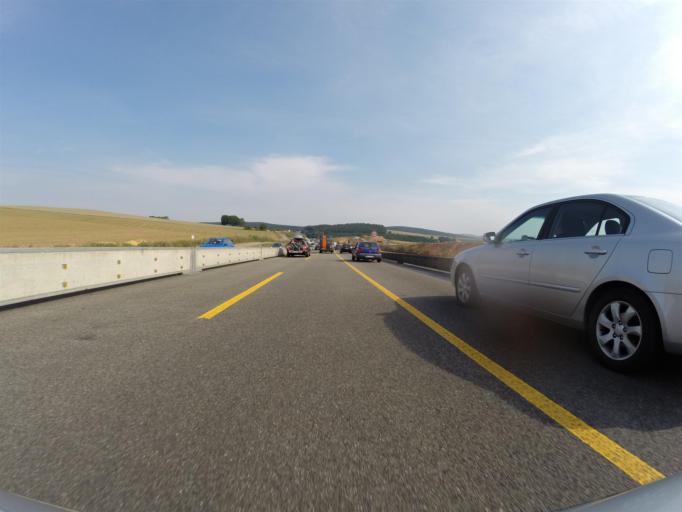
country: DE
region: Hesse
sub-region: Regierungsbezirk Kassel
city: Korle
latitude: 51.1442
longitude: 9.4756
